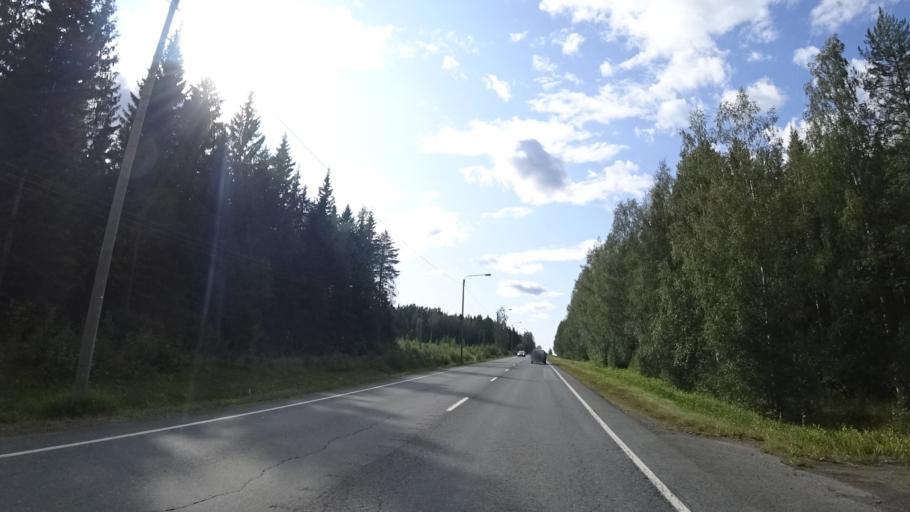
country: FI
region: North Karelia
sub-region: Keski-Karjala
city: Tohmajaervi
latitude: 62.2217
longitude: 30.3700
